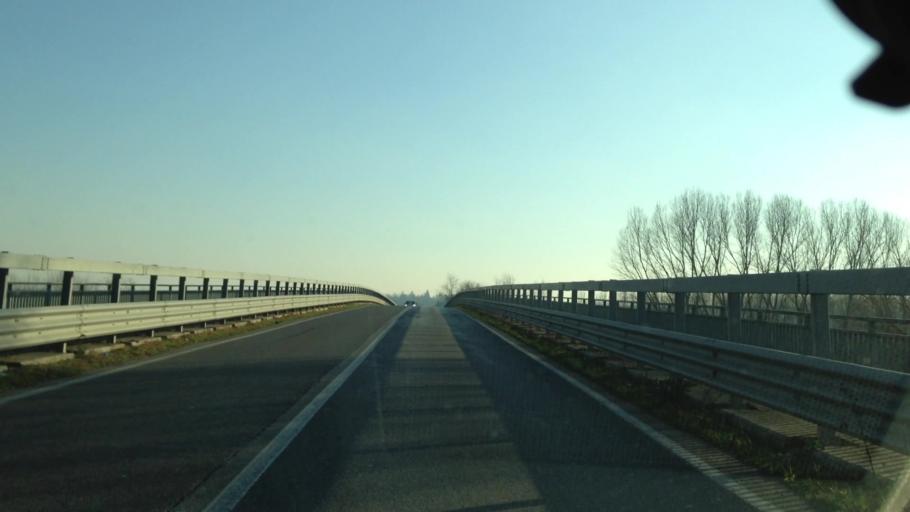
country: IT
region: Piedmont
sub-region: Provincia di Alessandria
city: Felizzano
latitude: 44.8910
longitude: 8.4387
